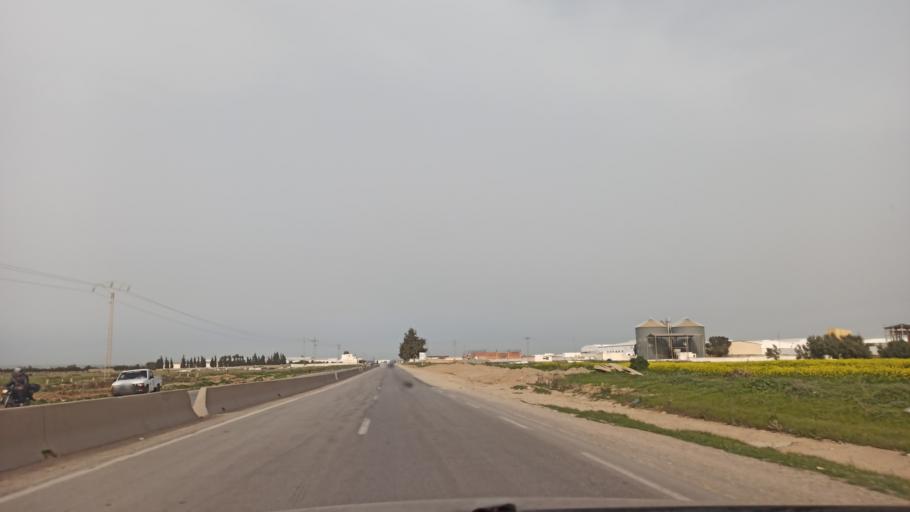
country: TN
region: Tunis
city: La Mohammedia
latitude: 36.5789
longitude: 10.0936
